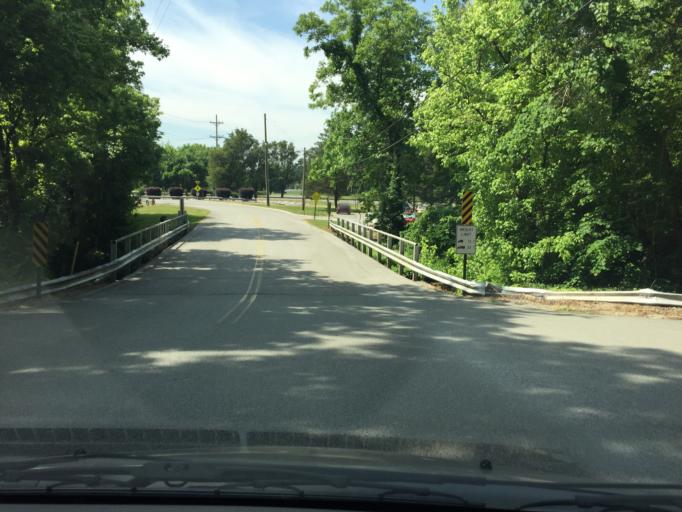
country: US
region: Tennessee
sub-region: Hamilton County
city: Collegedale
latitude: 35.0546
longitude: -85.0499
